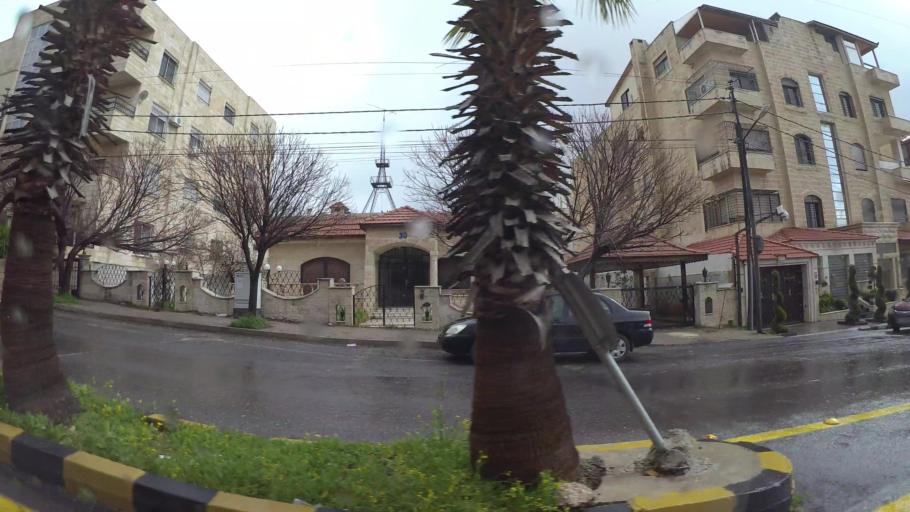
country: JO
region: Amman
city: Wadi as Sir
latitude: 31.9636
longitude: 35.8532
